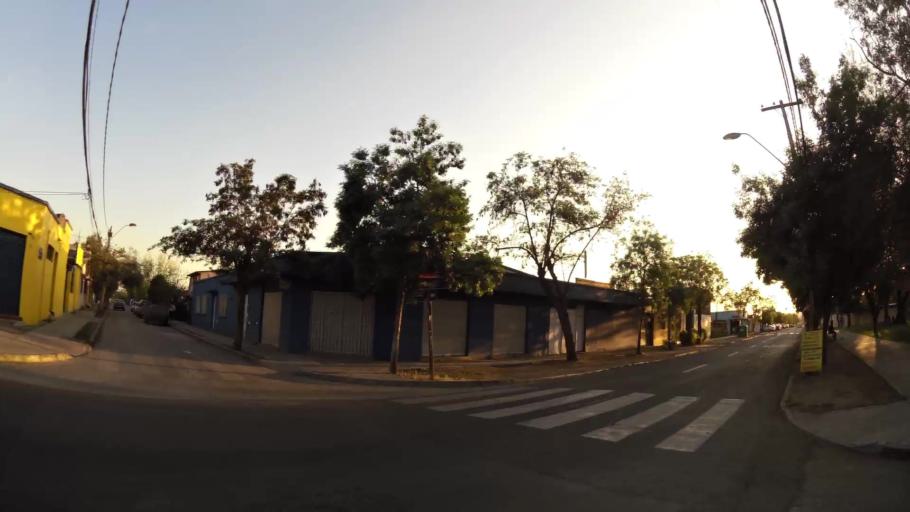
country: CL
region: Santiago Metropolitan
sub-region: Provincia de Santiago
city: Santiago
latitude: -33.5037
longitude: -70.6341
